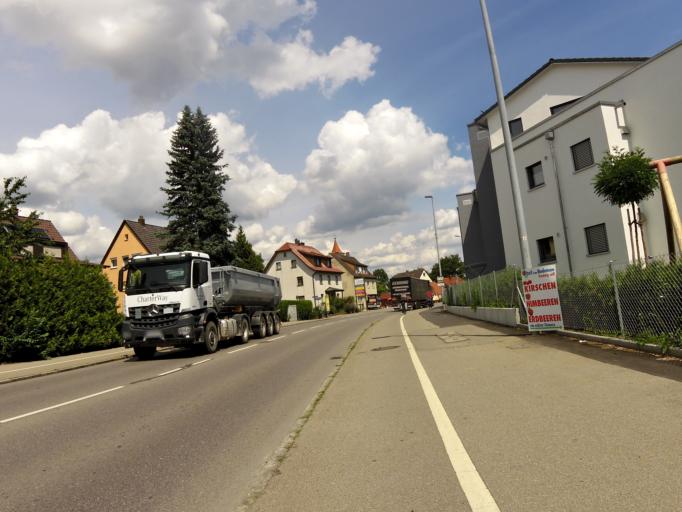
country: DE
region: Baden-Wuerttemberg
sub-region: Tuebingen Region
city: Immenstaad am Bodensee
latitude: 47.6700
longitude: 9.4057
